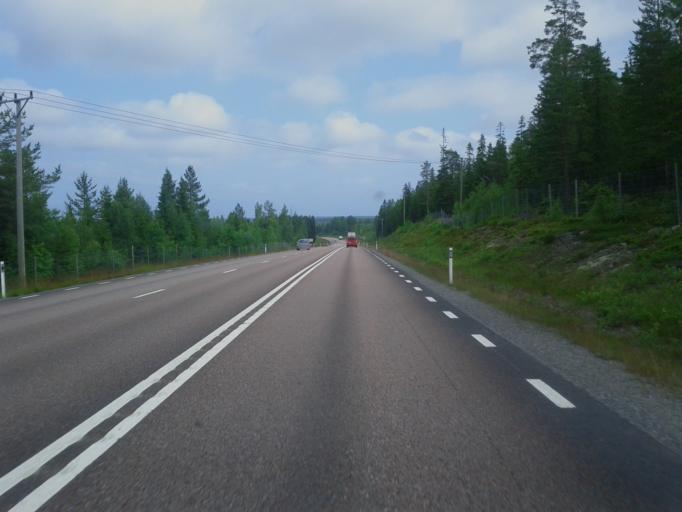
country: SE
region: Vaesterbotten
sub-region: Skelleftea Kommun
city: Burea
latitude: 64.4557
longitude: 21.2868
